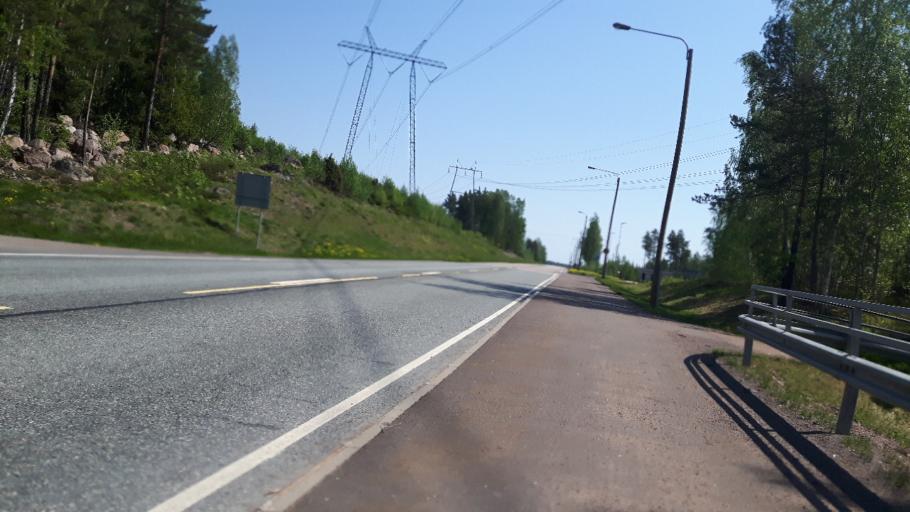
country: FI
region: Uusimaa
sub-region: Loviisa
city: Ruotsinpyhtaeae
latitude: 60.4928
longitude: 26.4520
